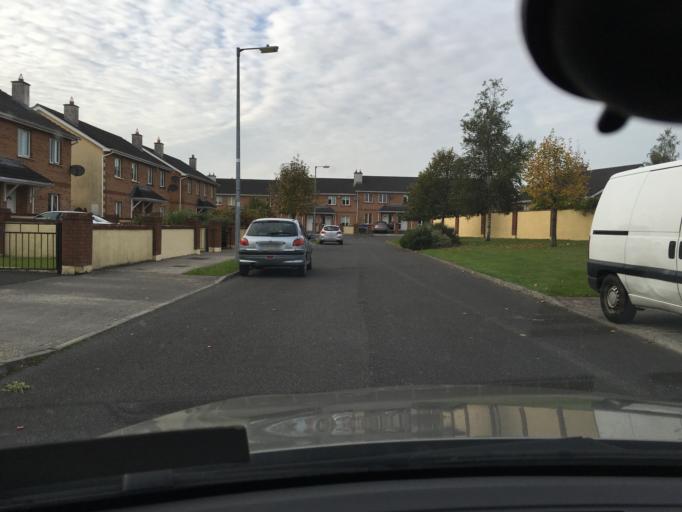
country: IE
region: Leinster
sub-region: An Longfort
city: Longford
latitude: 53.7222
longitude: -7.7991
